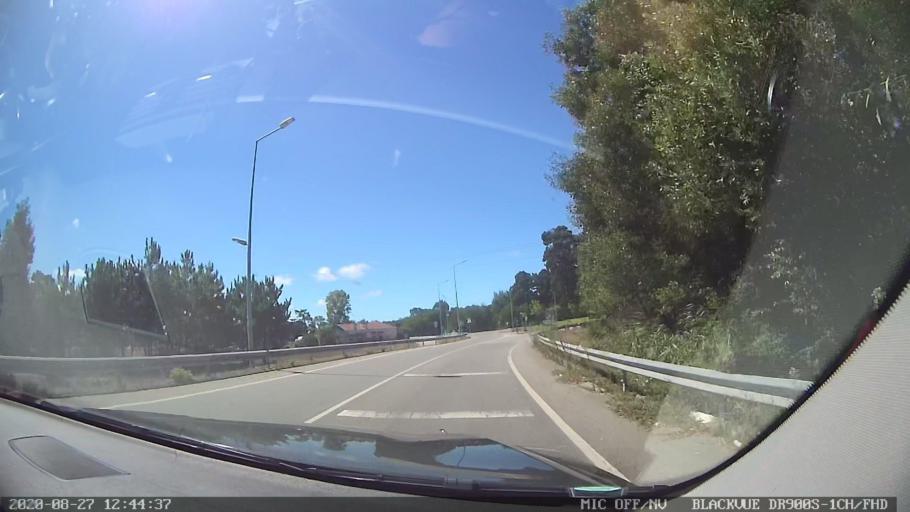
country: PT
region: Aveiro
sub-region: Ilhavo
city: Ilhavo
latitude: 40.6236
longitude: -8.6852
